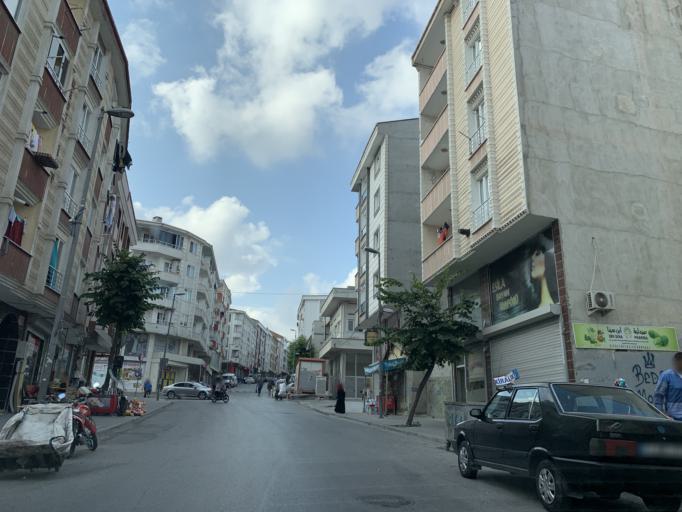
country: TR
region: Istanbul
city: Esenyurt
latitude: 41.0294
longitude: 28.6748
